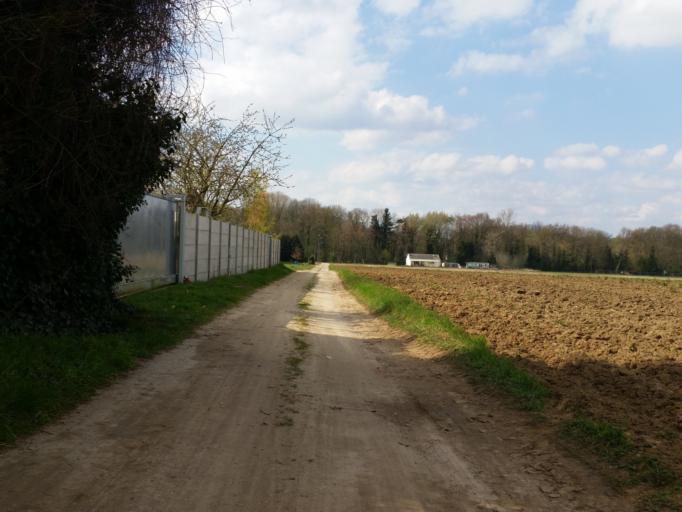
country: BE
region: Flanders
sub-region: Provincie Vlaams-Brabant
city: Kampenhout
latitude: 50.9242
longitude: 4.5559
